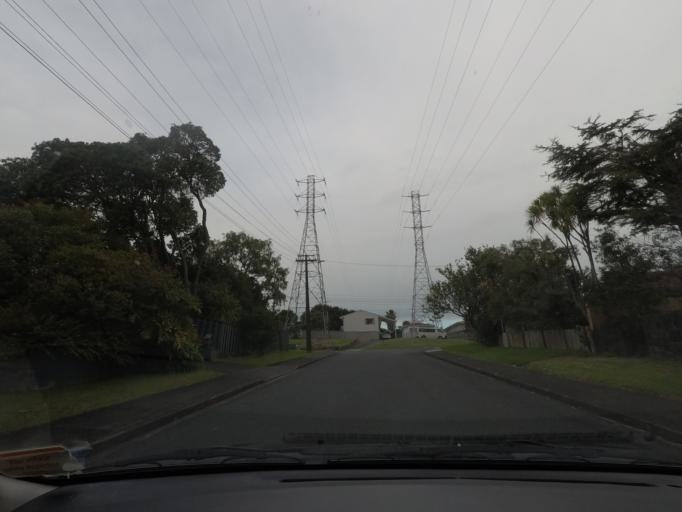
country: NZ
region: Auckland
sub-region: Auckland
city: Rosebank
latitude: -36.8553
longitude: 174.6435
